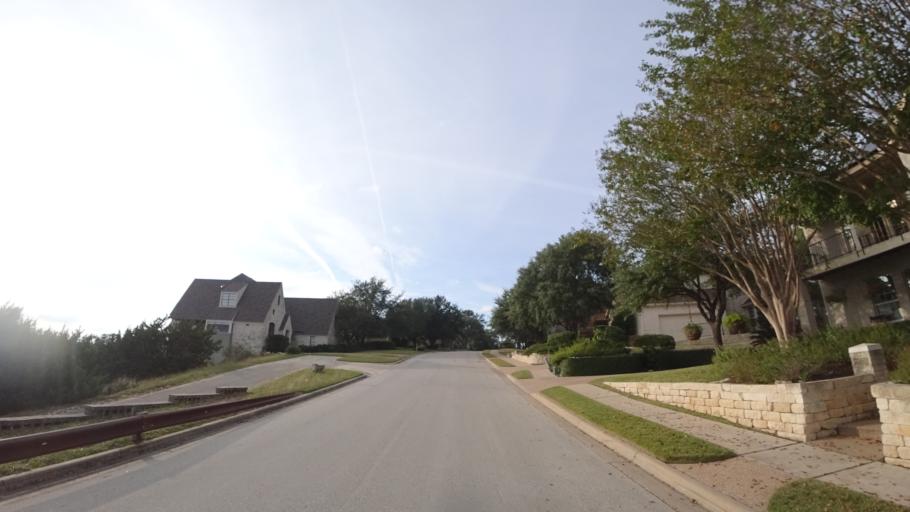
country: US
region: Texas
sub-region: Travis County
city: Hudson Bend
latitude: 30.3751
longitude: -97.8789
